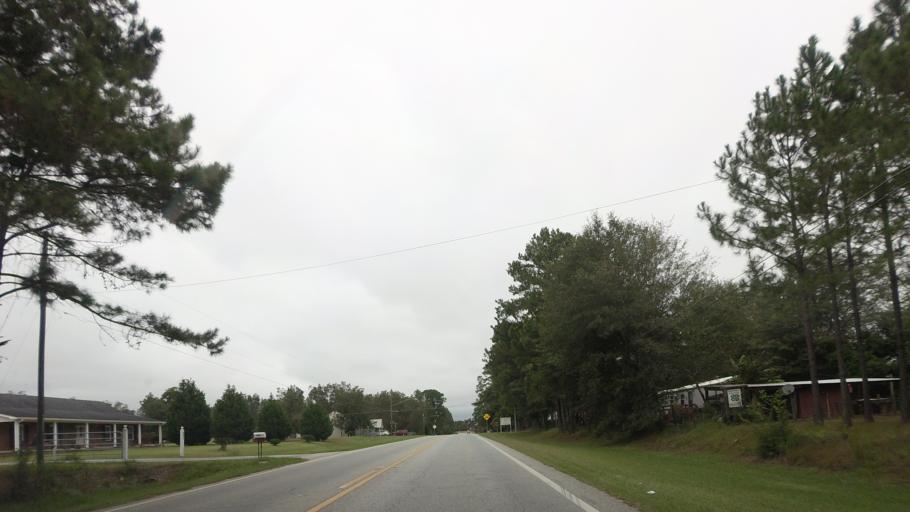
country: US
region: Georgia
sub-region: Berrien County
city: Ray City
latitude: 31.0686
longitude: -83.1978
